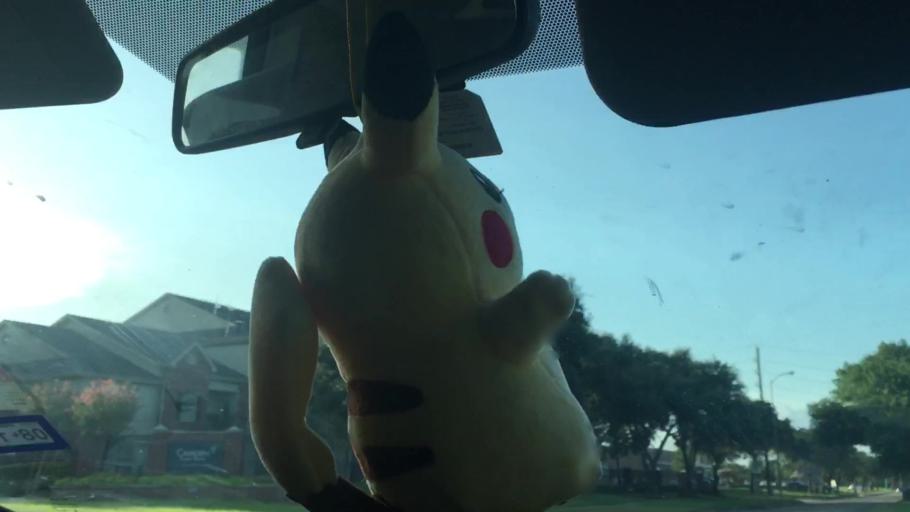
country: US
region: Texas
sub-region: Fort Bend County
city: Meadows Place
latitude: 29.6452
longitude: -95.5821
